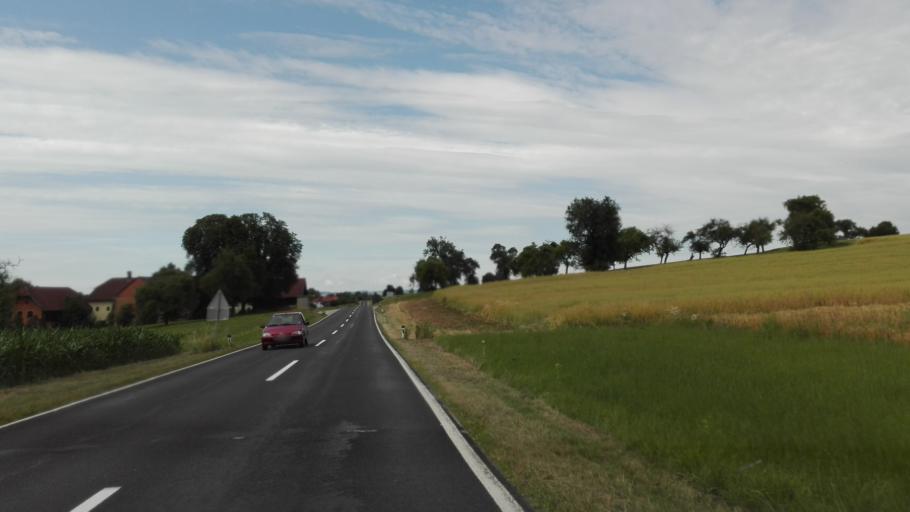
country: AT
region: Upper Austria
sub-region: Politischer Bezirk Grieskirchen
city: Grieskirchen
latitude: 48.2712
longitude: 13.8200
